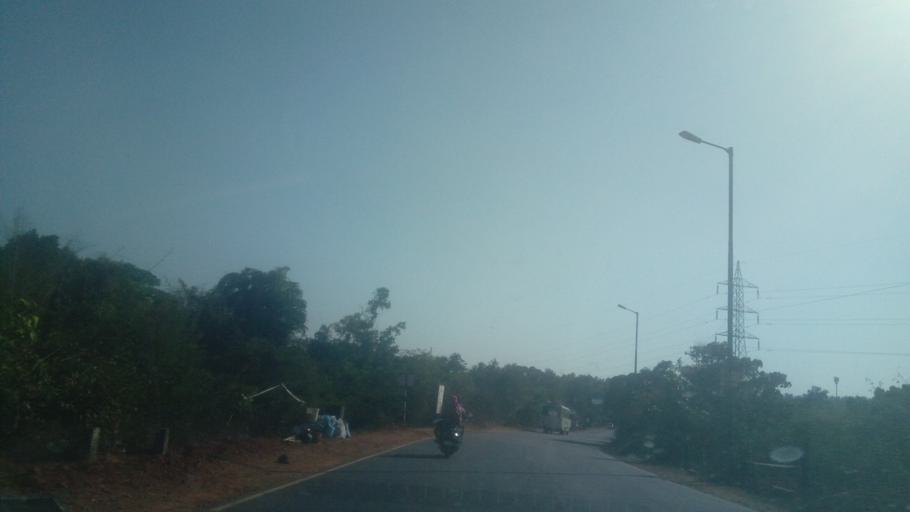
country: IN
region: Goa
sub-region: North Goa
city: Jua
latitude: 15.5262
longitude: 73.9665
